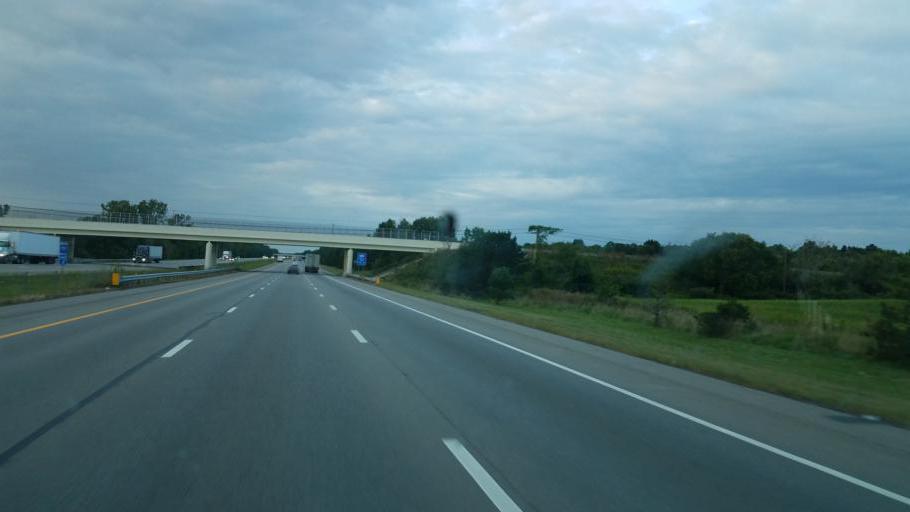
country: US
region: Ohio
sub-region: Morrow County
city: Cardington
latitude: 40.3992
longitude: -82.8226
